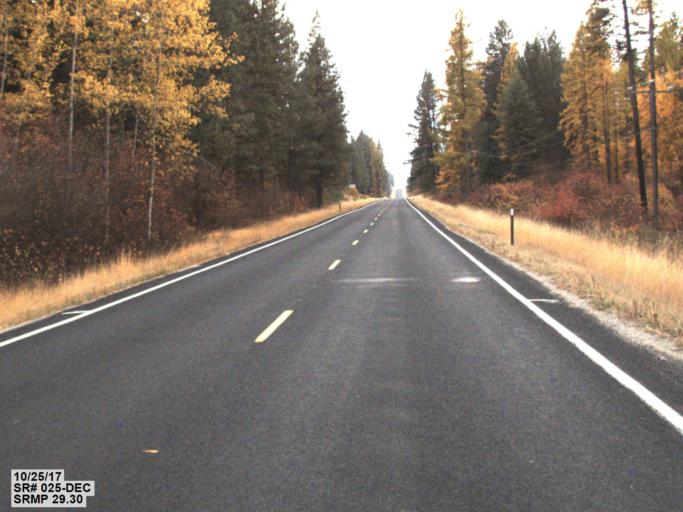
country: US
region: Washington
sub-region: Lincoln County
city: Davenport
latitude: 47.9736
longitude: -118.2998
